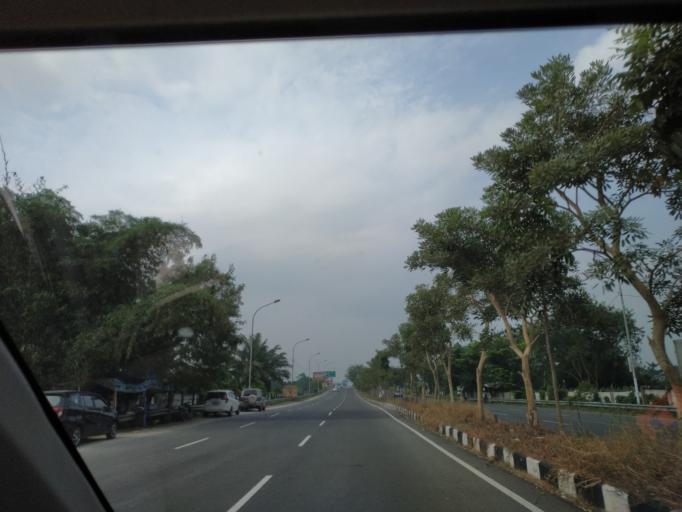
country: ID
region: North Sumatra
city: Percut
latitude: 3.6042
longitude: 98.8481
